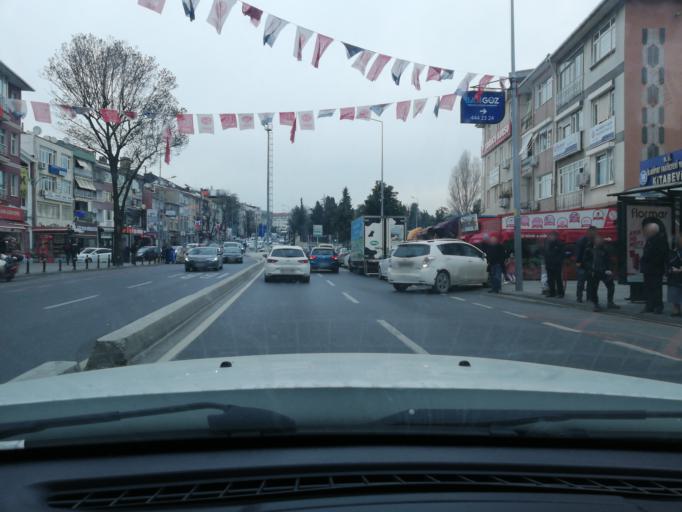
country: TR
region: Istanbul
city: UEskuedar
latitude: 41.0206
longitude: 29.0350
